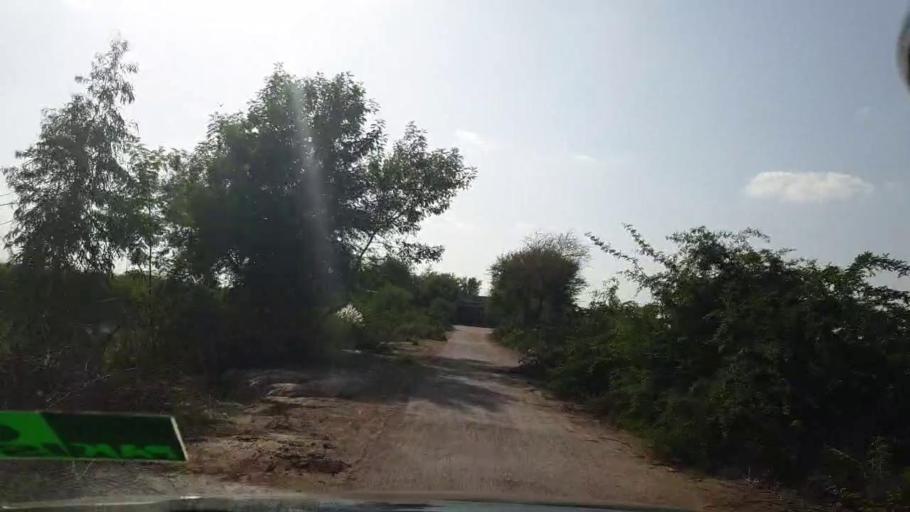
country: PK
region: Sindh
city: Tando Bago
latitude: 24.7118
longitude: 69.1938
